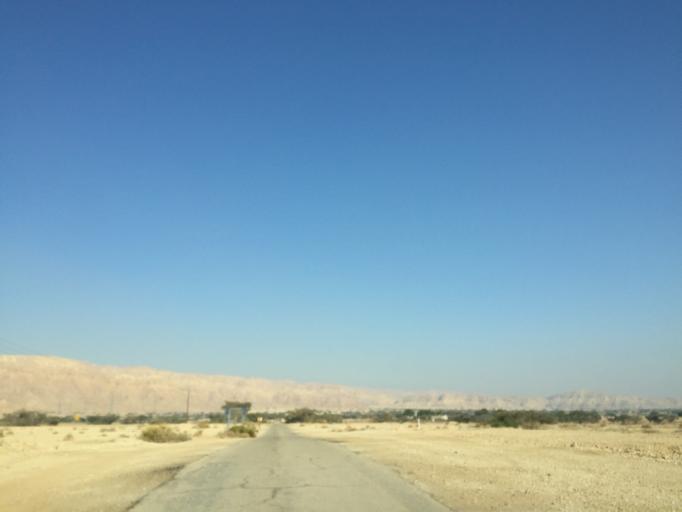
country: JO
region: Ma'an
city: Al Quwayrah
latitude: 29.8419
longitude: 35.0299
